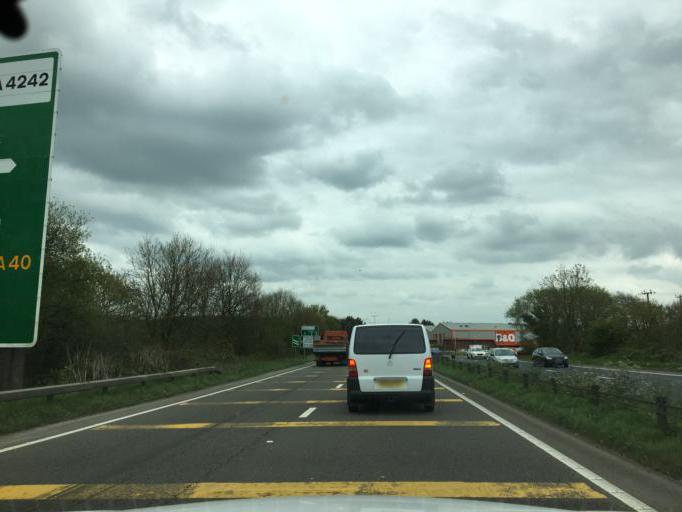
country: GB
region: Wales
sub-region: Carmarthenshire
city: Carmarthen
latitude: 51.8514
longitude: -4.3200
